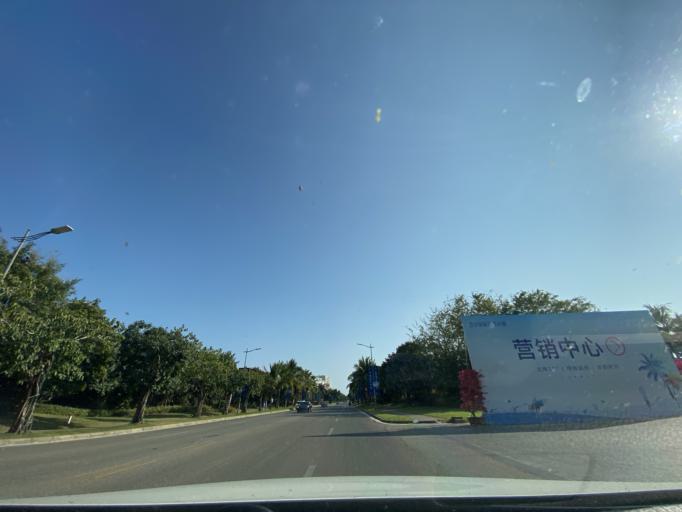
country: CN
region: Hainan
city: Xincun
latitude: 18.4203
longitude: 109.9611
